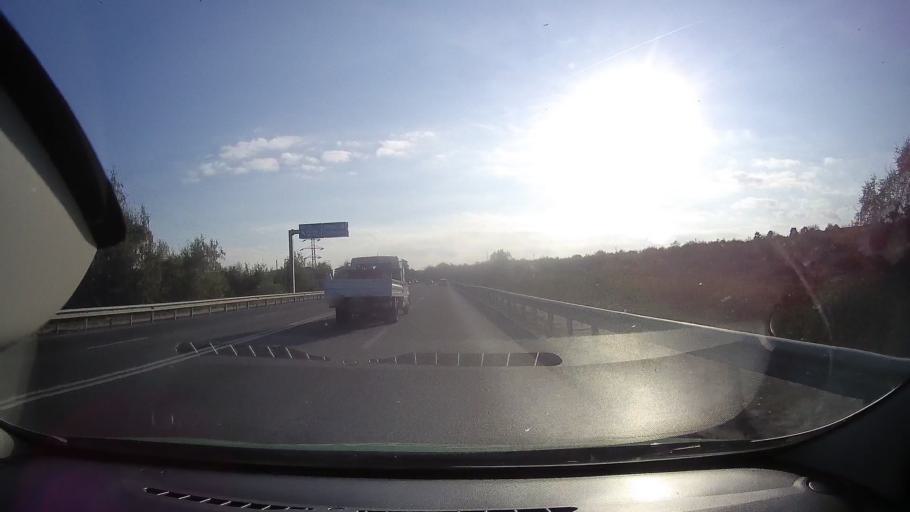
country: RO
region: Constanta
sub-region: Comuna Ovidiu
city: Ovidiu
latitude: 44.2665
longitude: 28.5553
